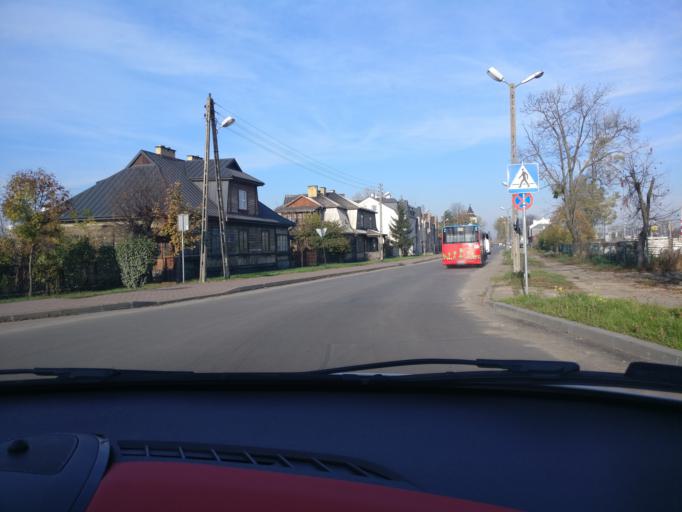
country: PL
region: Lublin Voivodeship
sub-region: Powiat rycki
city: Deblin
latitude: 51.5758
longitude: 21.8371
